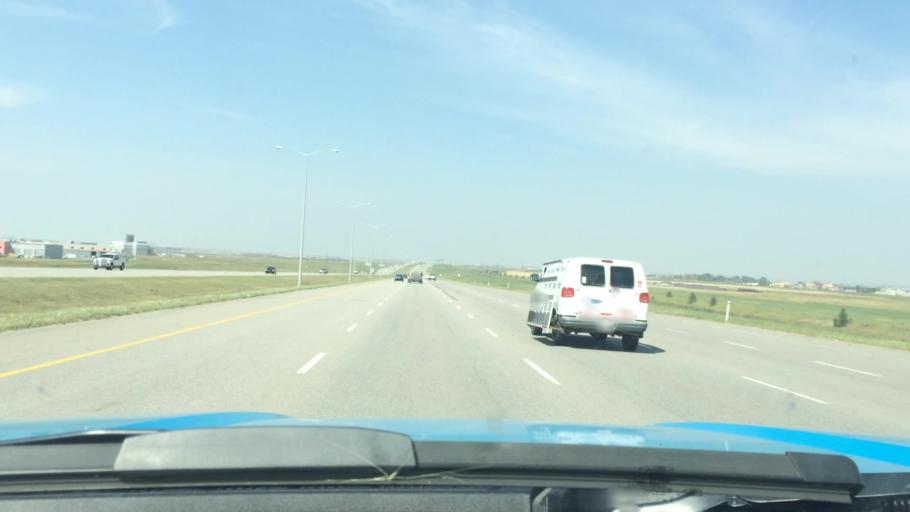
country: CA
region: Alberta
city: Chestermere
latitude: 50.9545
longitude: -113.9205
